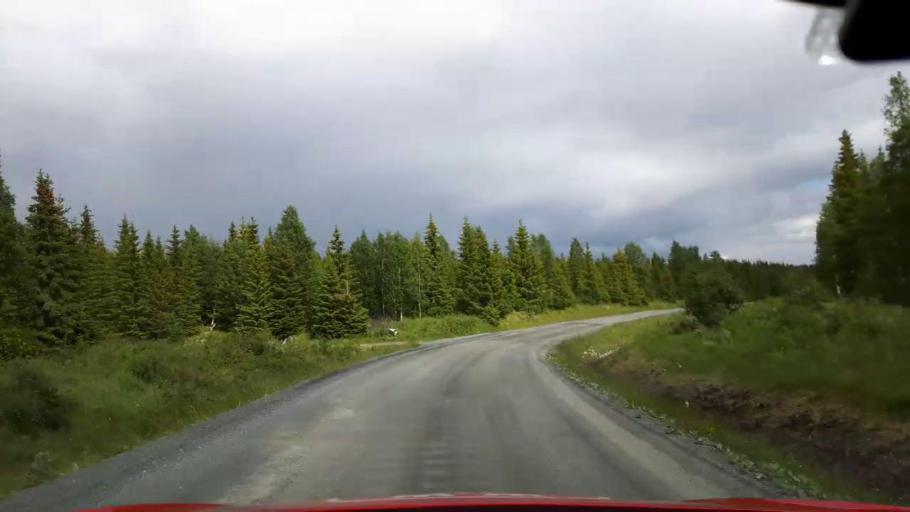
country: NO
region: Nord-Trondelag
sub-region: Lierne
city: Sandvika
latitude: 64.1448
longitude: 13.9201
